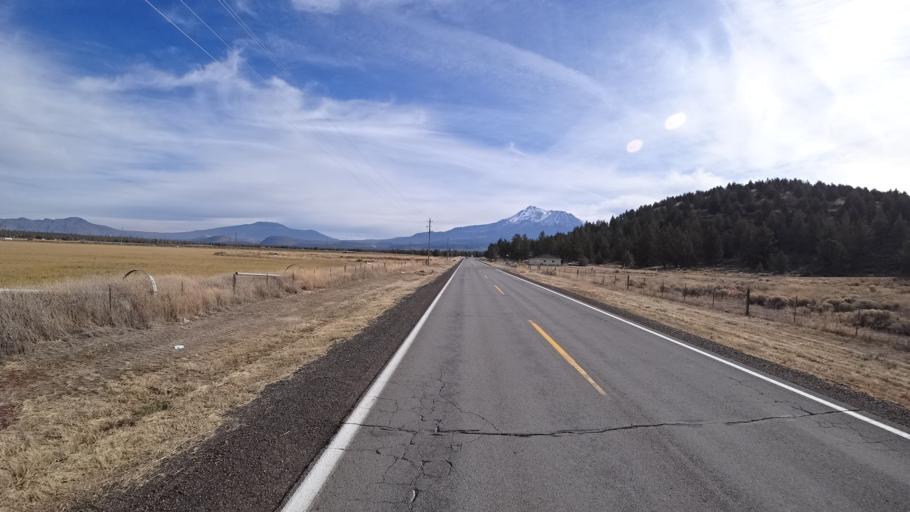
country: US
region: California
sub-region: Siskiyou County
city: Weed
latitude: 41.5430
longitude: -122.3695
